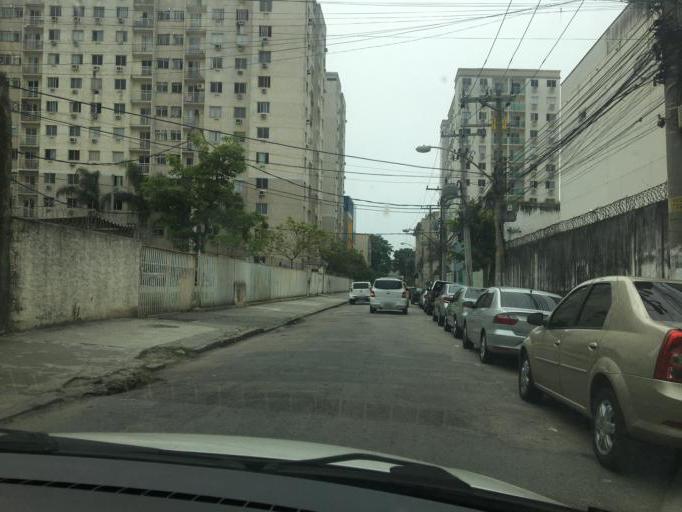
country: BR
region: Rio de Janeiro
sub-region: Rio De Janeiro
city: Rio de Janeiro
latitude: -22.8933
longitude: -43.2202
